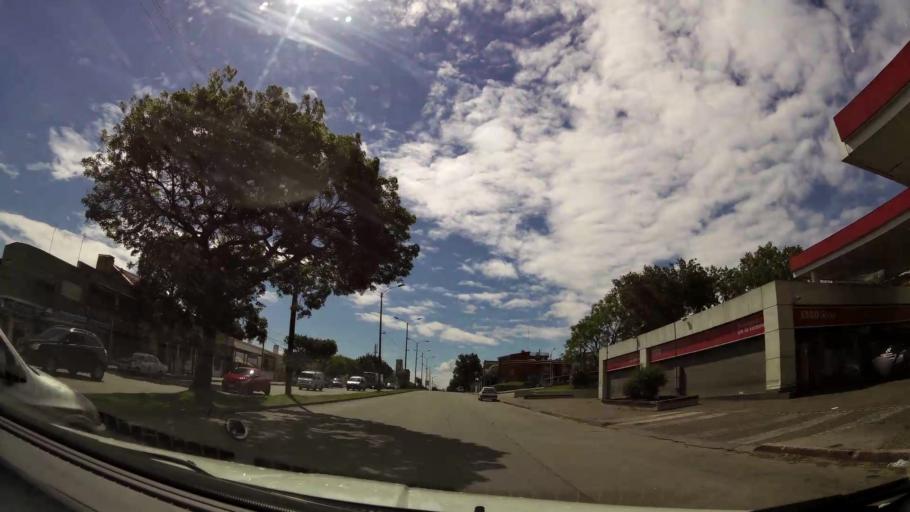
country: UY
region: Montevideo
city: Montevideo
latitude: -34.8613
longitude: -56.1714
